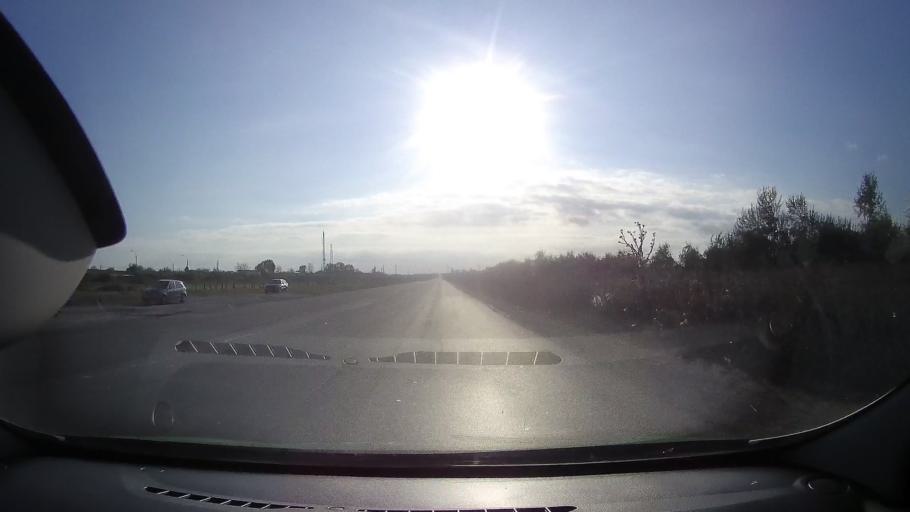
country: RO
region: Constanta
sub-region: Comuna Navodari
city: Navodari
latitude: 44.3386
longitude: 28.6367
